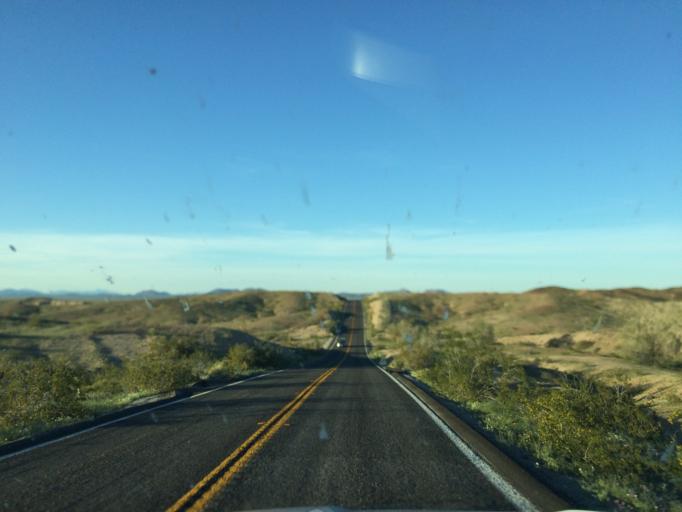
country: US
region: California
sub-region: Riverside County
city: Mesa Verde
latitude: 33.2030
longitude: -114.8570
